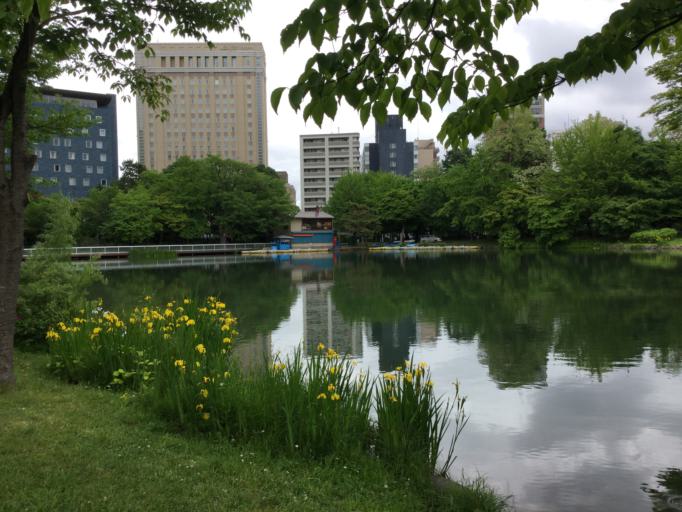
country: JP
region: Hokkaido
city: Sapporo
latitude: 43.0465
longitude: 141.3542
